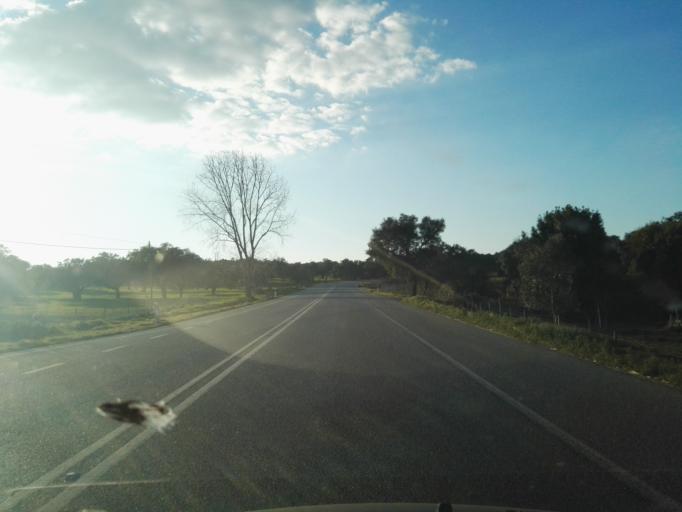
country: PT
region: Evora
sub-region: Arraiolos
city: Arraiolos
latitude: 38.6136
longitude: -8.0749
